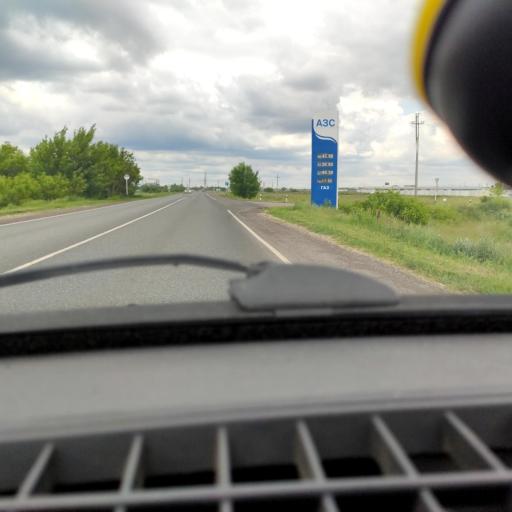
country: RU
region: Samara
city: Povolzhskiy
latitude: 53.6508
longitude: 49.6854
